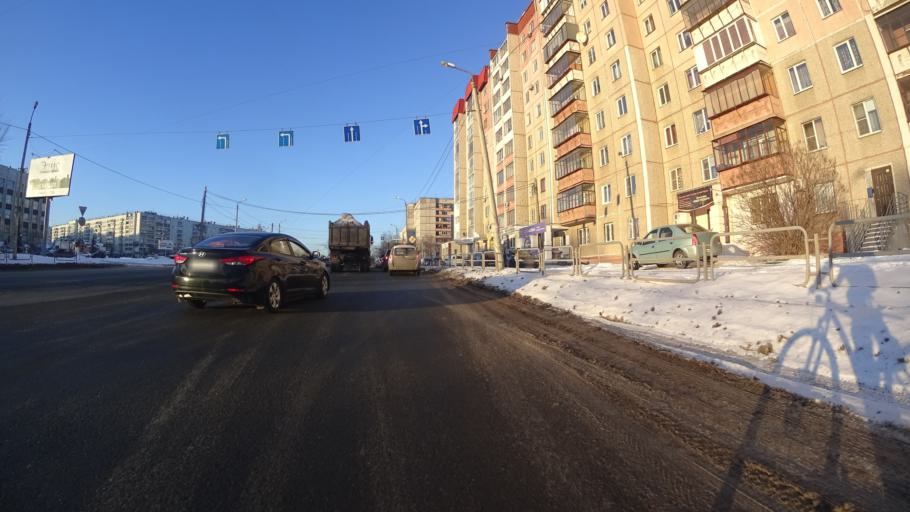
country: RU
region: Chelyabinsk
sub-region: Gorod Chelyabinsk
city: Chelyabinsk
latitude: 55.1907
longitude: 61.3635
